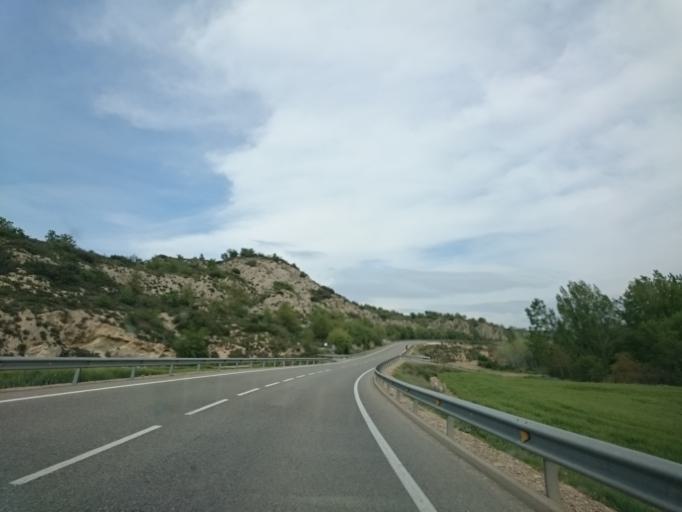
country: ES
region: Catalonia
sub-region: Provincia de Lleida
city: Tora de Riubregos
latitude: 41.8263
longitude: 1.3288
